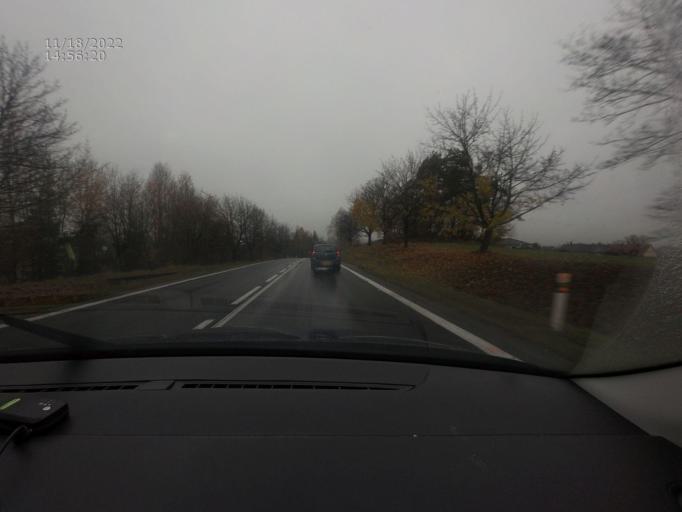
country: CZ
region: Jihocesky
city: Kovarov
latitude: 49.4728
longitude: 14.2959
